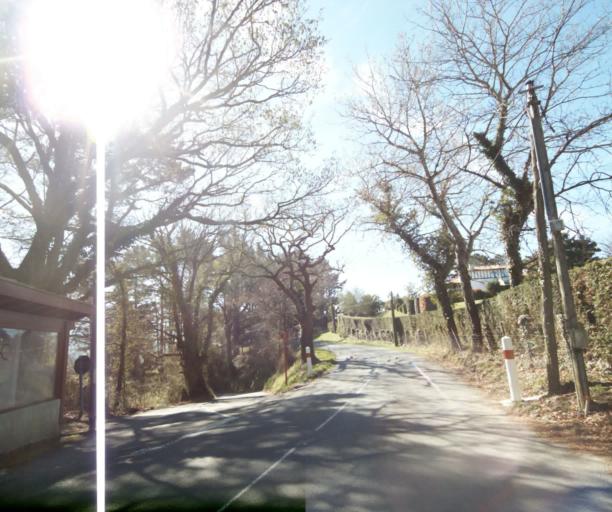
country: FR
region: Aquitaine
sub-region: Departement des Pyrenees-Atlantiques
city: Ciboure
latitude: 43.3528
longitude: -1.6672
